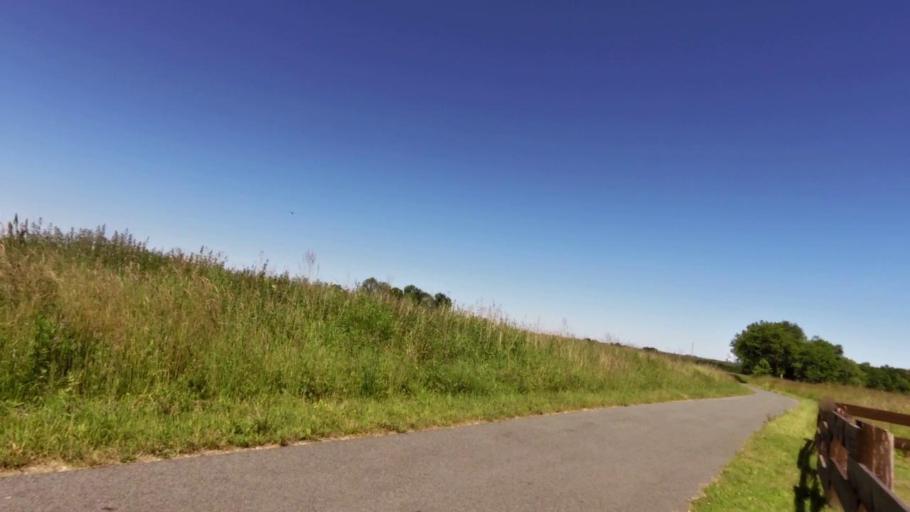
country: PL
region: West Pomeranian Voivodeship
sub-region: Powiat bialogardzki
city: Karlino
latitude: 54.0595
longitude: 15.8451
